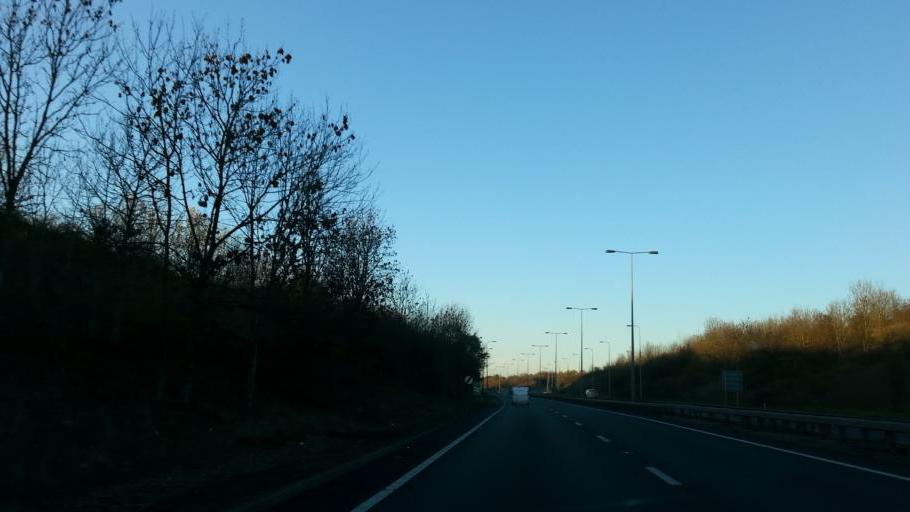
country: GB
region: England
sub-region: Cambridgeshire
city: Great Stukeley
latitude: 52.3664
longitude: -0.2386
